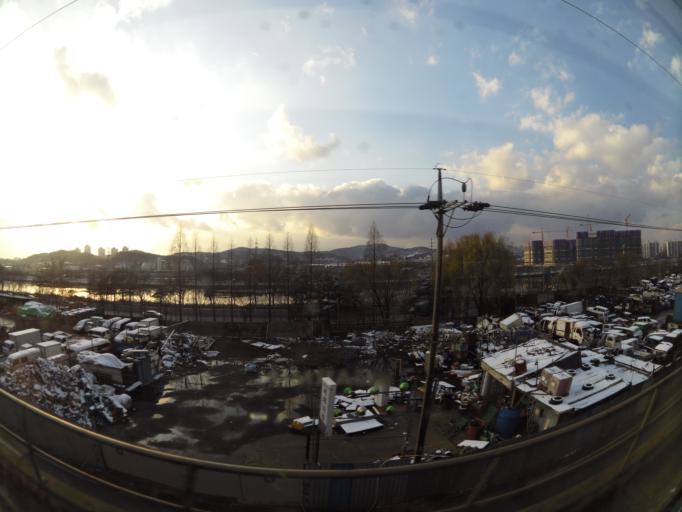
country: KR
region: Daejeon
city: Songgang-dong
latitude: 36.3883
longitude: 127.4136
